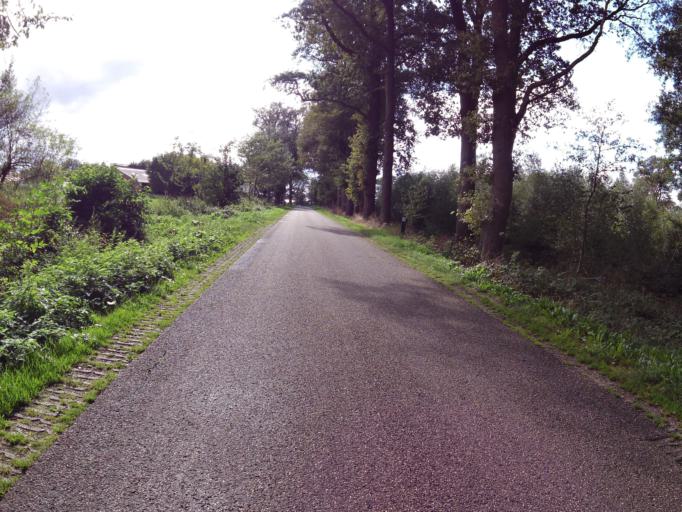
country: NL
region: Gelderland
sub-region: Gemeente Aalten
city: Bredevoort
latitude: 51.9606
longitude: 6.6268
